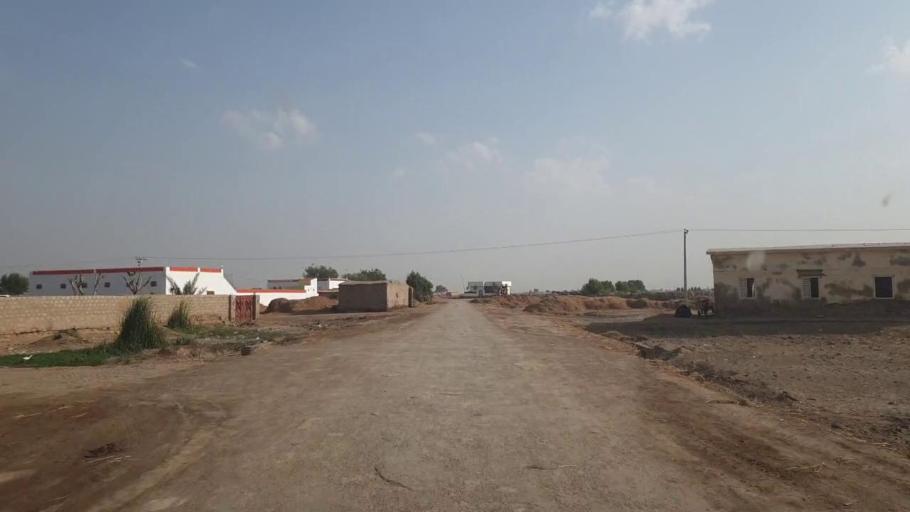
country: PK
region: Sindh
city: Kario
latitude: 24.5808
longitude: 68.5412
